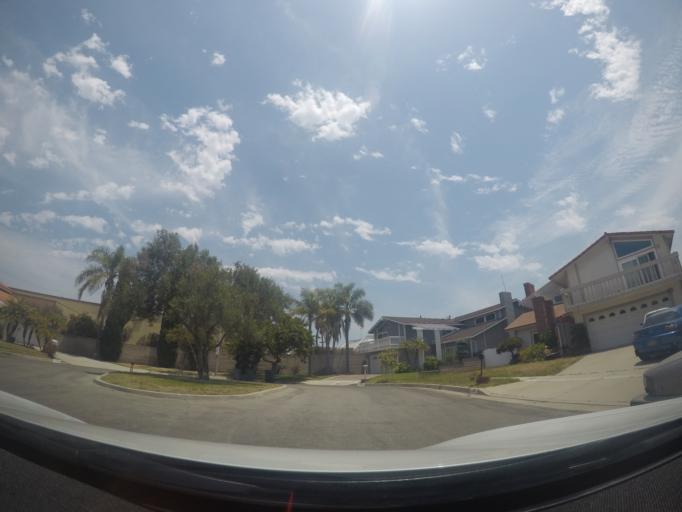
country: US
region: California
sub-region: Los Angeles County
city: Torrance
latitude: 33.8193
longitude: -118.3528
